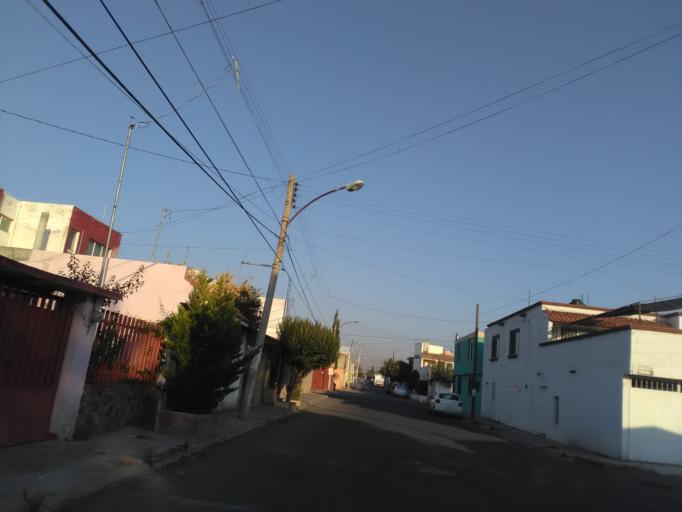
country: MX
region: Durango
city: Victoria de Durango
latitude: 24.0381
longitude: -104.6383
